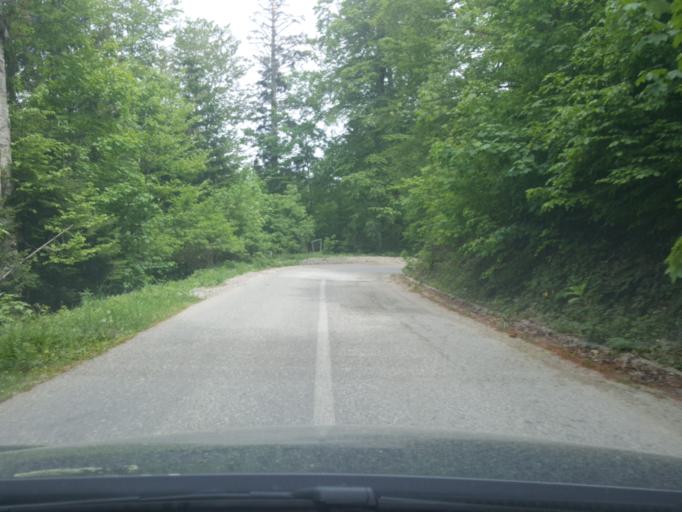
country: RS
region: Central Serbia
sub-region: Zlatiborski Okrug
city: Bajina Basta
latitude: 43.9128
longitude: 19.4960
